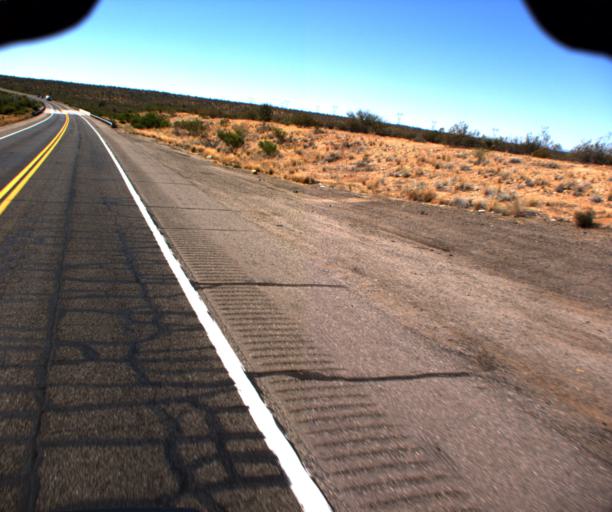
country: US
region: Arizona
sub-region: Yavapai County
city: Congress
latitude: 34.2076
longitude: -113.0647
